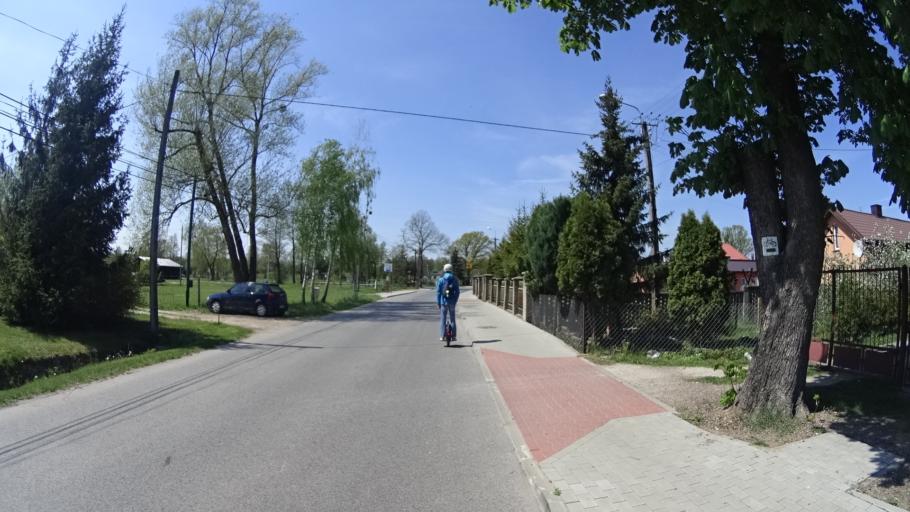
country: PL
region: Masovian Voivodeship
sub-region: Powiat warszawski zachodni
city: Truskaw
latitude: 52.2838
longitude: 20.7311
